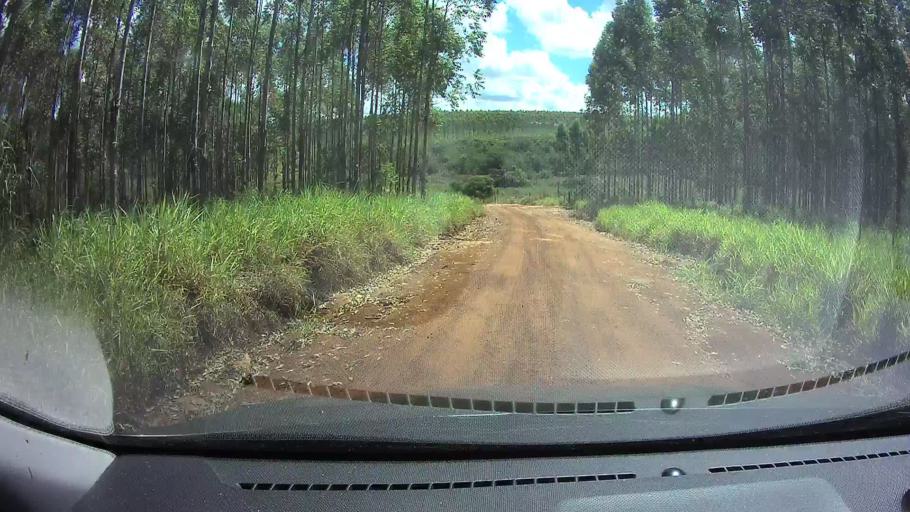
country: PY
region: Paraguari
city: La Colmena
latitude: -25.9636
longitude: -56.7390
